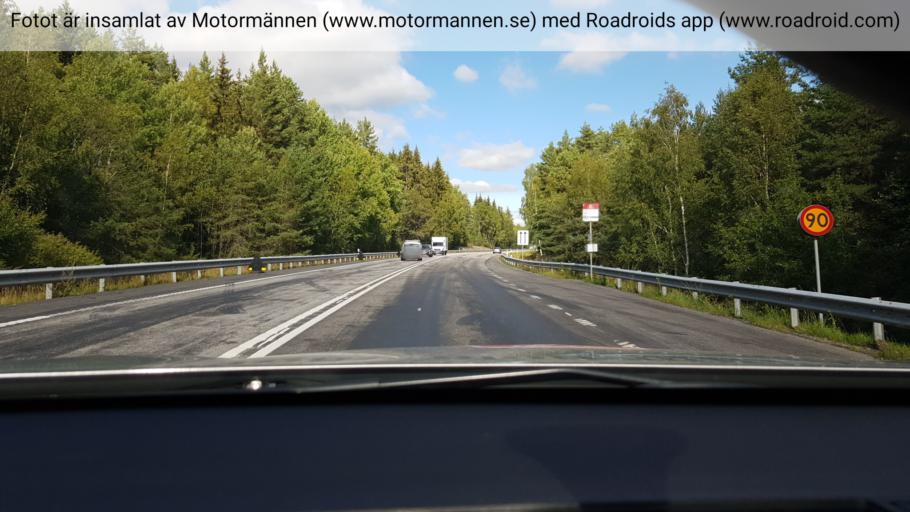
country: SE
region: Stockholm
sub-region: Lidingo
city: Brevik
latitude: 59.4344
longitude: 18.2194
